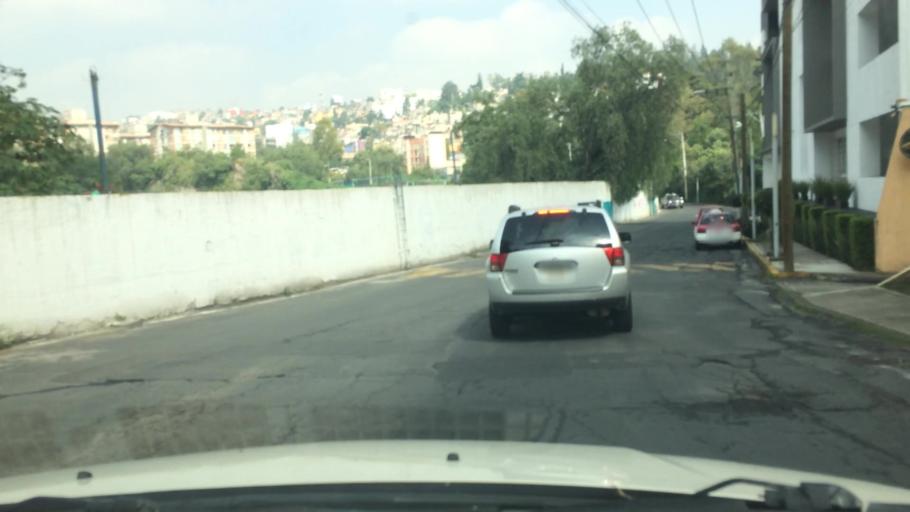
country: MX
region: Mexico City
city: Magdalena Contreras
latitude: 19.3464
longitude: -99.2130
